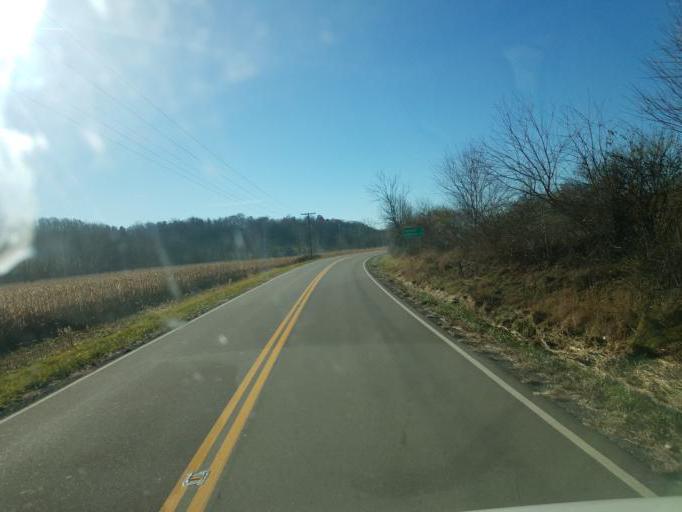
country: US
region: Ohio
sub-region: Muskingum County
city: Dresden
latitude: 40.2525
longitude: -82.0498
